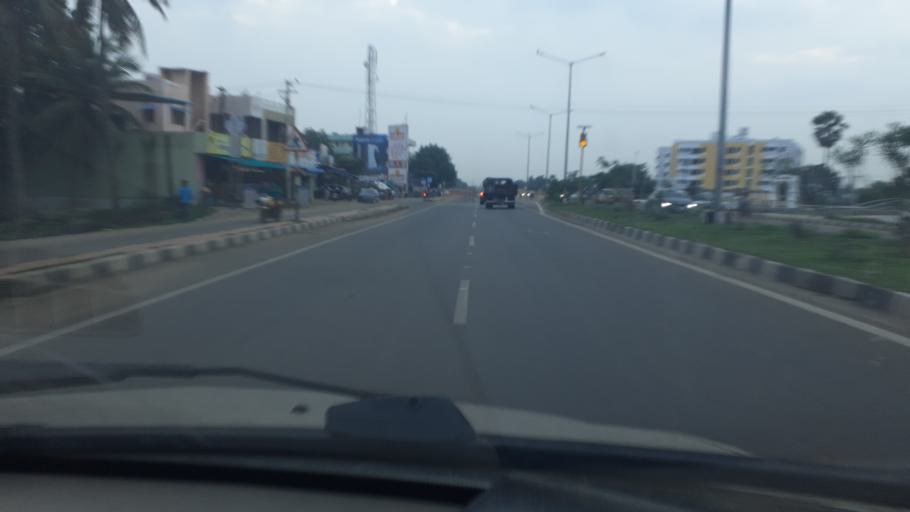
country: IN
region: Tamil Nadu
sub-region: Thoothukkudi
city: Korampallam
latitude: 8.7830
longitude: 78.1021
